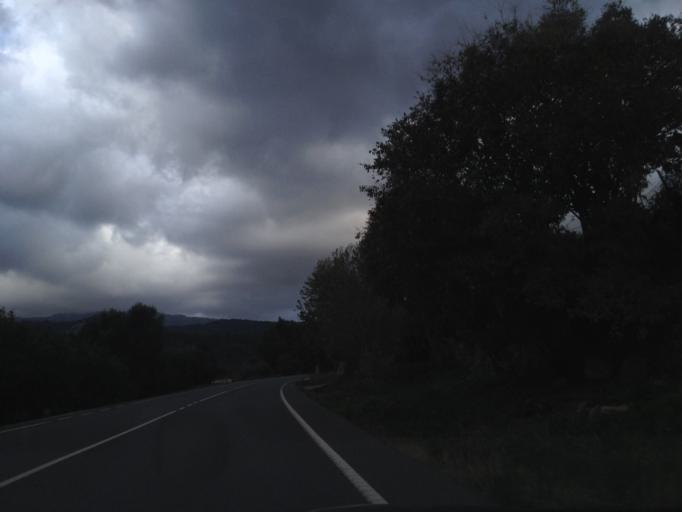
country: ES
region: Balearic Islands
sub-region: Illes Balears
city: Pollenca
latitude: 39.8652
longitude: 3.0150
